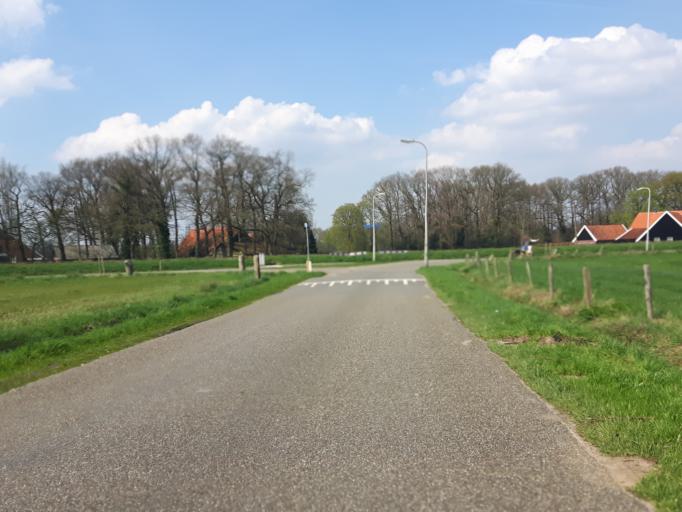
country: NL
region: Overijssel
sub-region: Gemeente Hengelo
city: Hengelo
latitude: 52.1980
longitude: 6.7940
